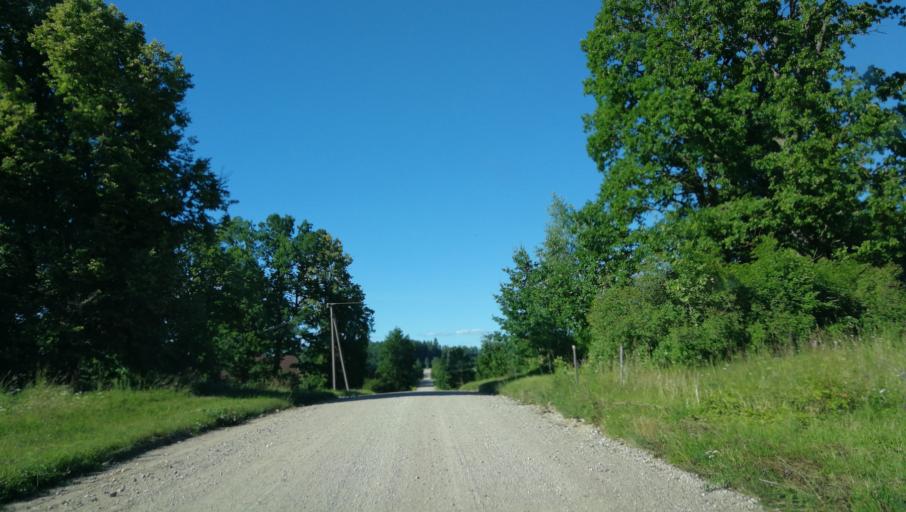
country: LV
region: Jaunpiebalga
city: Jaunpiebalga
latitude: 56.9996
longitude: 26.0298
